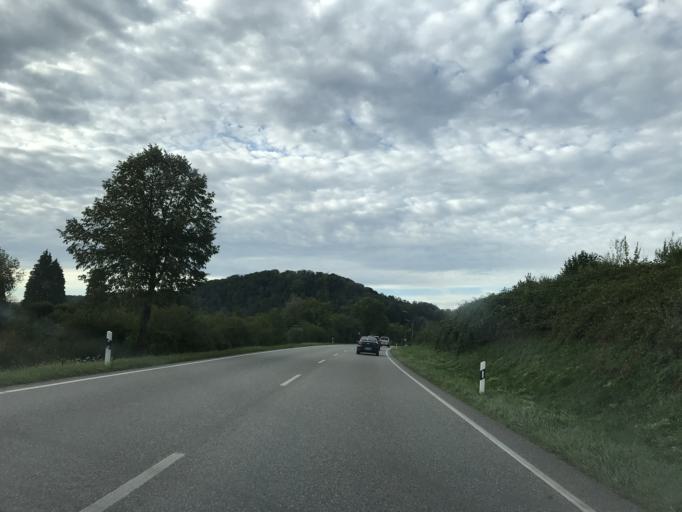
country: CH
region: Aargau
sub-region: Bezirk Rheinfelden
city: Mumpf
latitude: 47.5789
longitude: 7.9116
